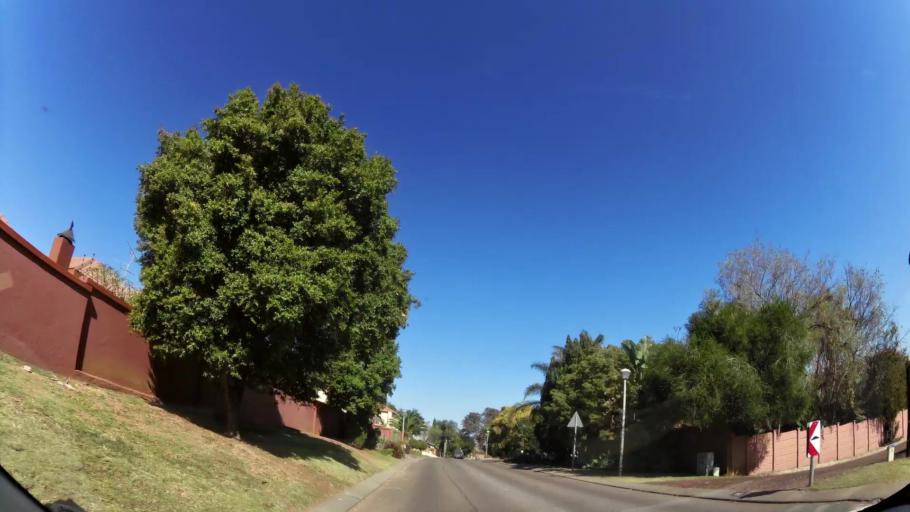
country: ZA
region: Gauteng
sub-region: City of Tshwane Metropolitan Municipality
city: Centurion
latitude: -25.8630
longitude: 28.1778
